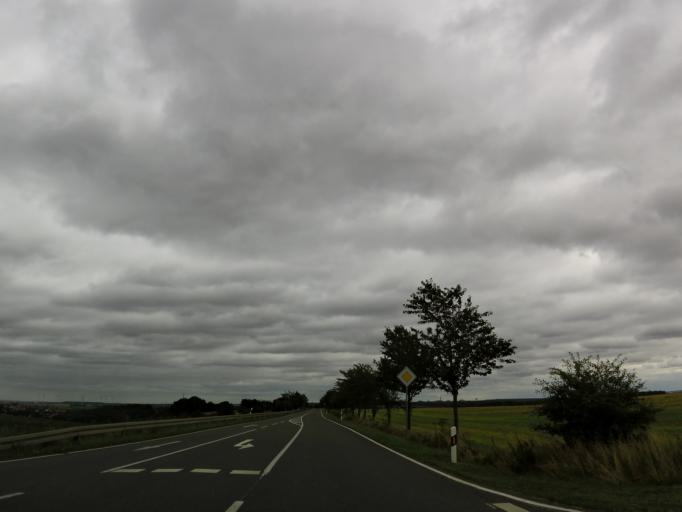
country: DE
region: Saxony-Anhalt
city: Teuchern
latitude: 51.1042
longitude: 12.0015
